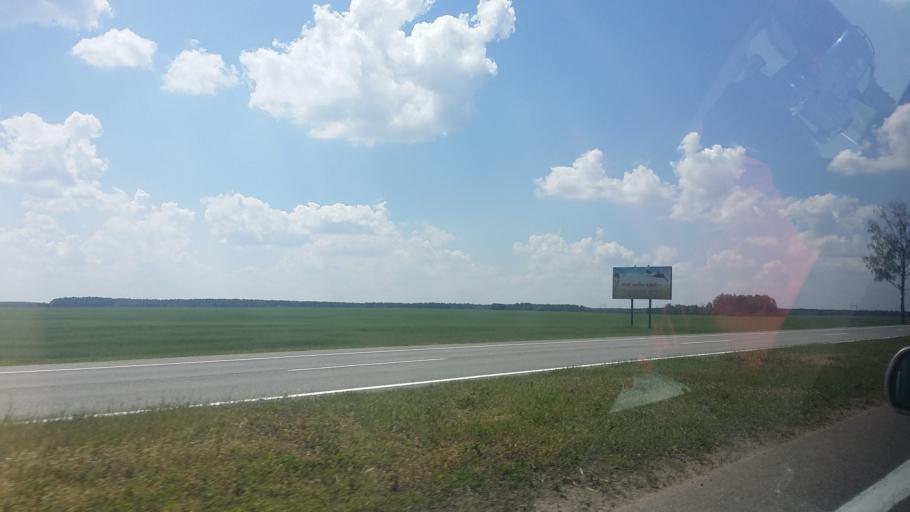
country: BY
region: Minsk
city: Smilavichy
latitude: 53.7642
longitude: 28.1427
